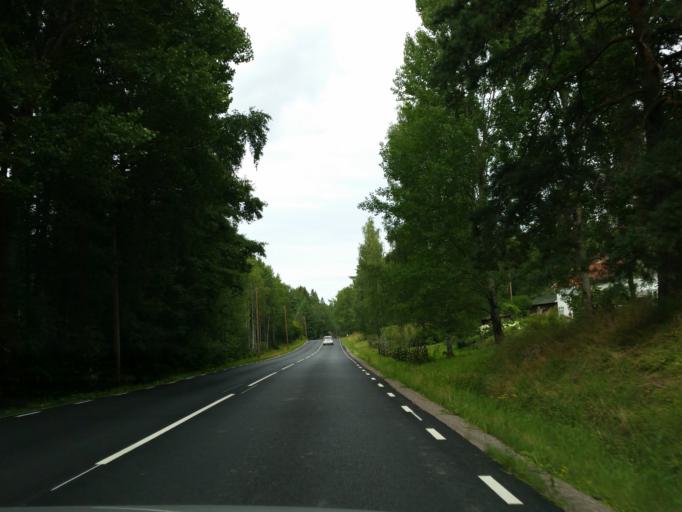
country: SE
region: Soedermanland
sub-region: Strangnas Kommun
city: Mariefred
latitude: 59.2641
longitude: 17.1624
